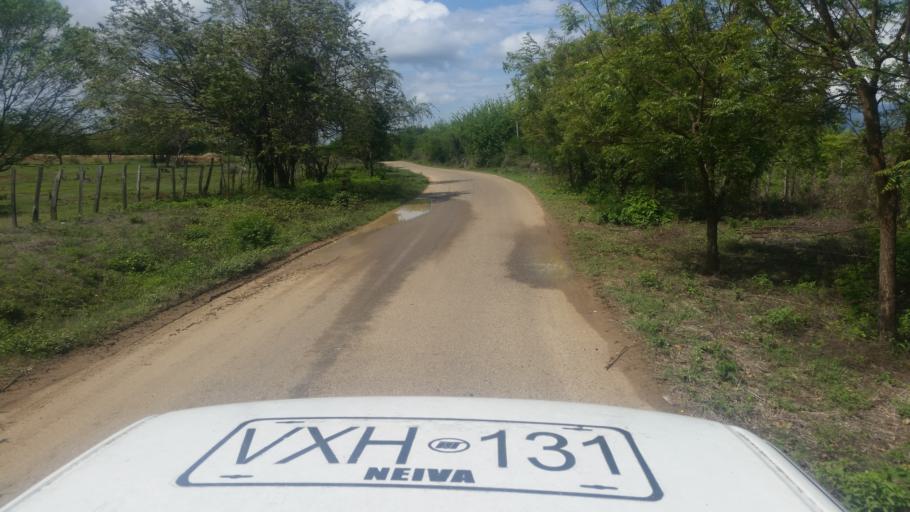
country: CO
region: Huila
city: Villavieja
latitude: 3.1984
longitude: -75.2115
